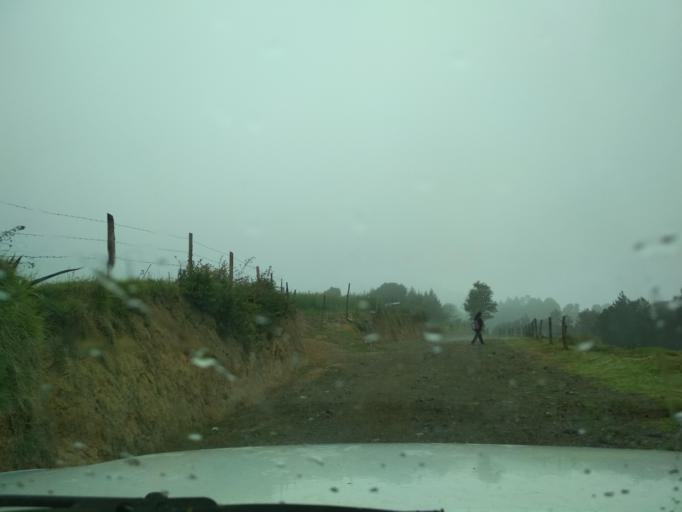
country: MX
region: Veracruz
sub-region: Mariano Escobedo
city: Loma Grande
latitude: 18.9272
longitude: -97.2193
